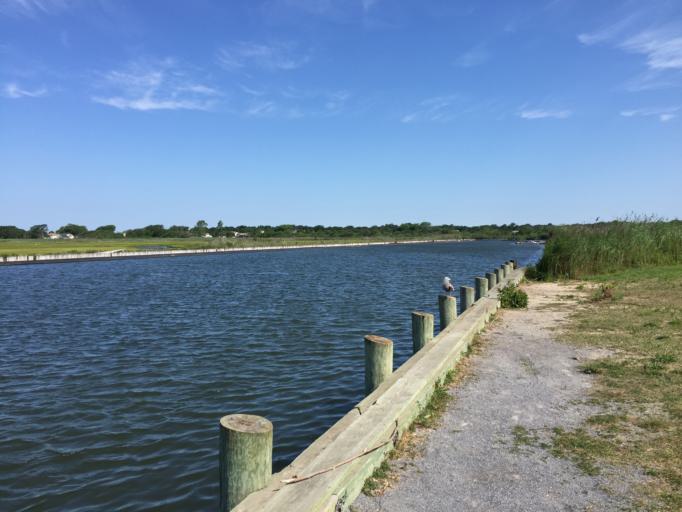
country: US
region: New York
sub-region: Suffolk County
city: Mastic Beach
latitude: 40.7408
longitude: -72.8736
